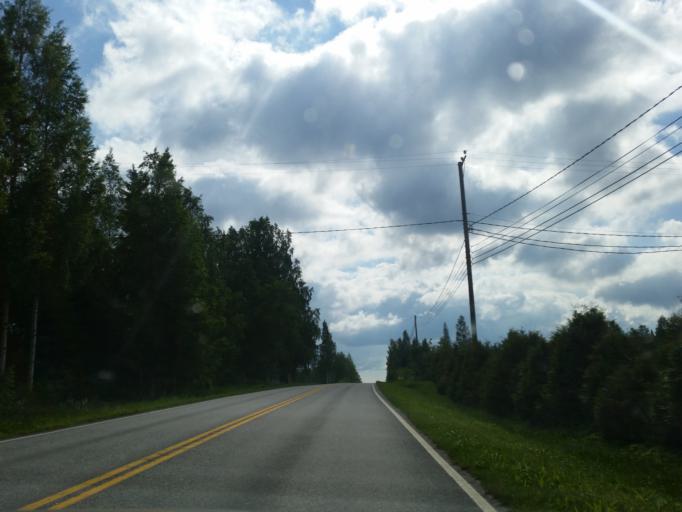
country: FI
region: Northern Savo
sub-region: Kuopio
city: Kuopio
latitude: 62.8470
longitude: 27.3956
